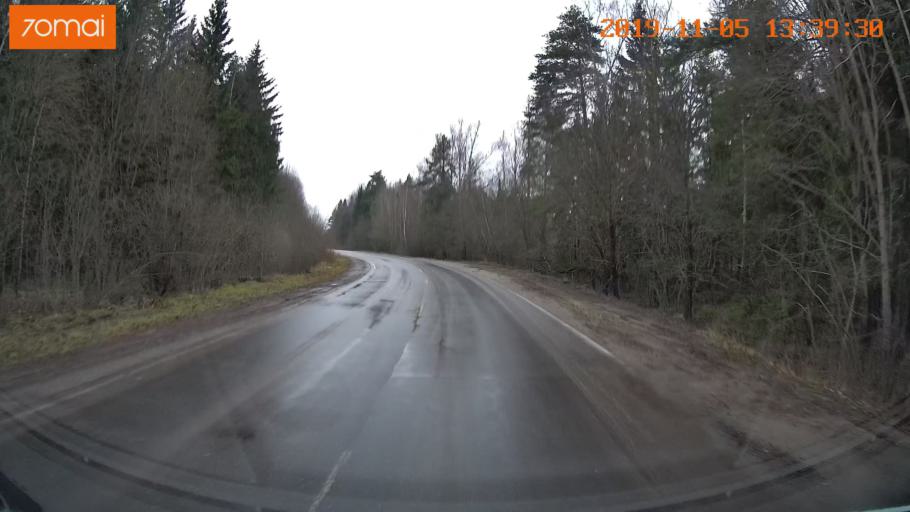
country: RU
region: Ivanovo
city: Shuya
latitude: 56.9402
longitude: 41.3865
